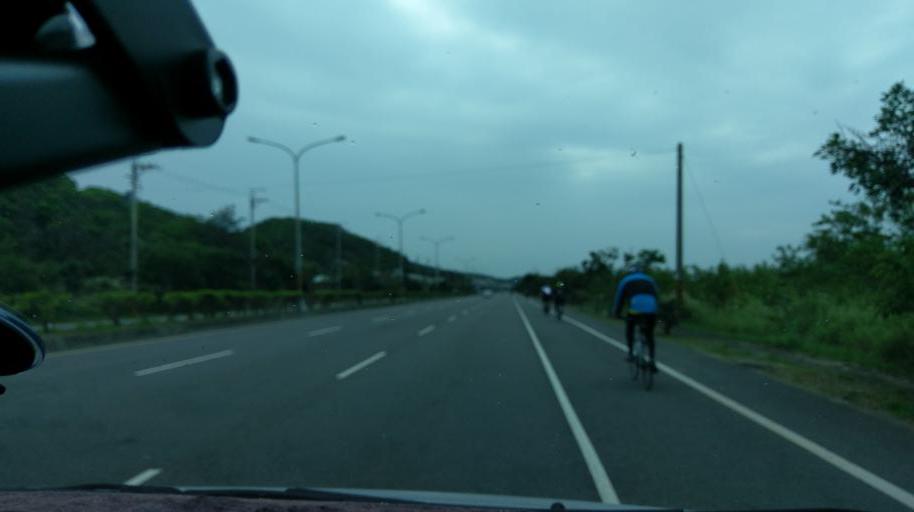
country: TW
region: Taiwan
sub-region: Miaoli
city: Miaoli
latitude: 24.5230
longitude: 120.6922
